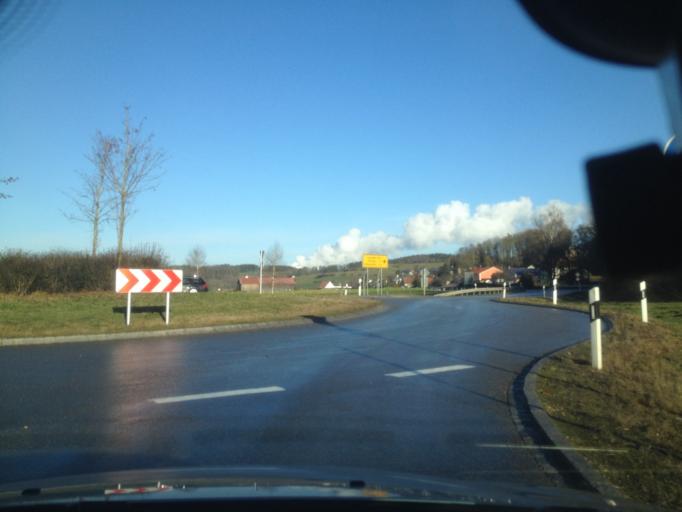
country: DE
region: Bavaria
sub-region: Swabia
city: Burgau
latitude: 48.4434
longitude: 10.4271
